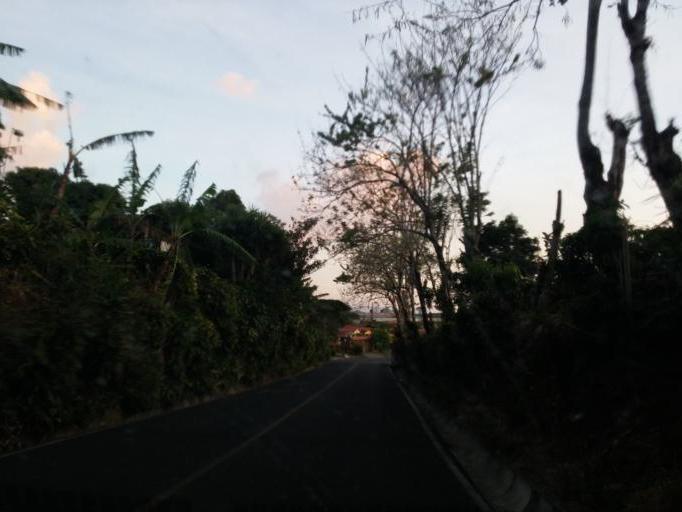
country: CR
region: Alajuela
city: Sabanilla
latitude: 10.0723
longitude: -84.2169
